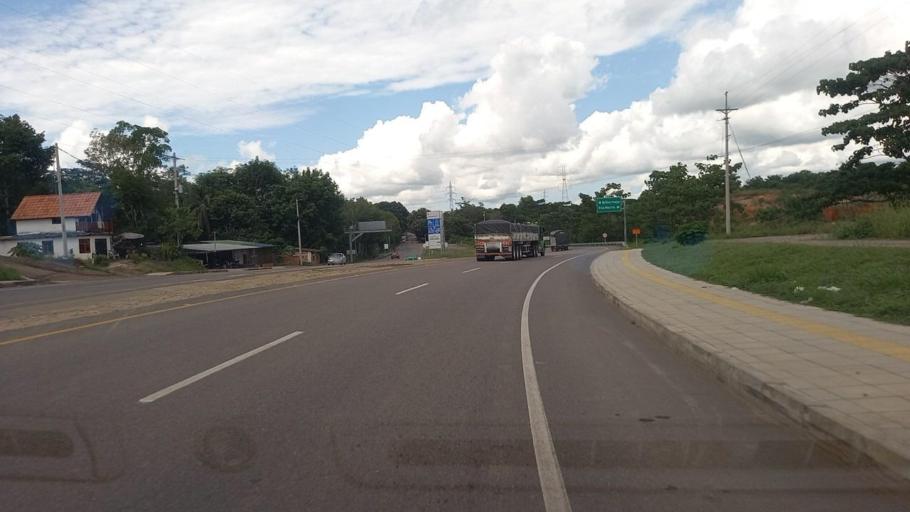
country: CO
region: Santander
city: Sabana de Torres
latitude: 7.1324
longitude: -73.5569
